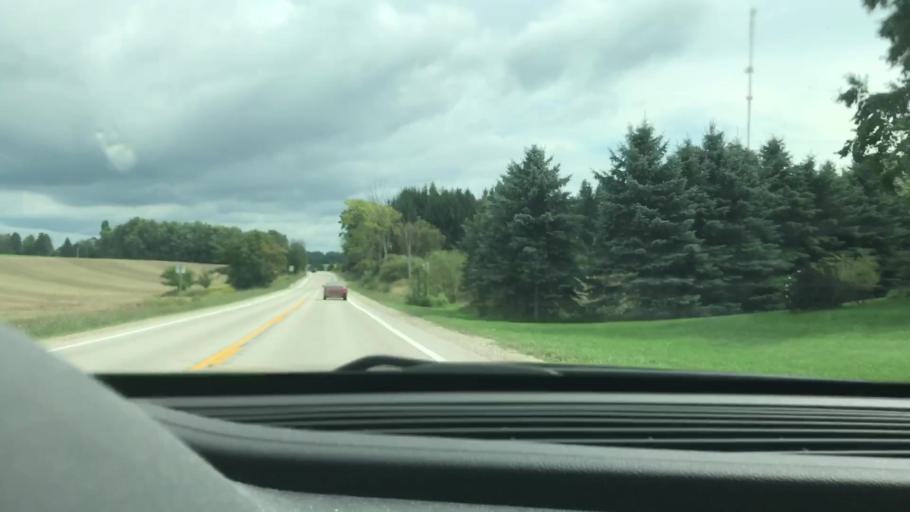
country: US
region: Michigan
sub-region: Antrim County
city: Bellaire
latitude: 45.0961
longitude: -85.2978
